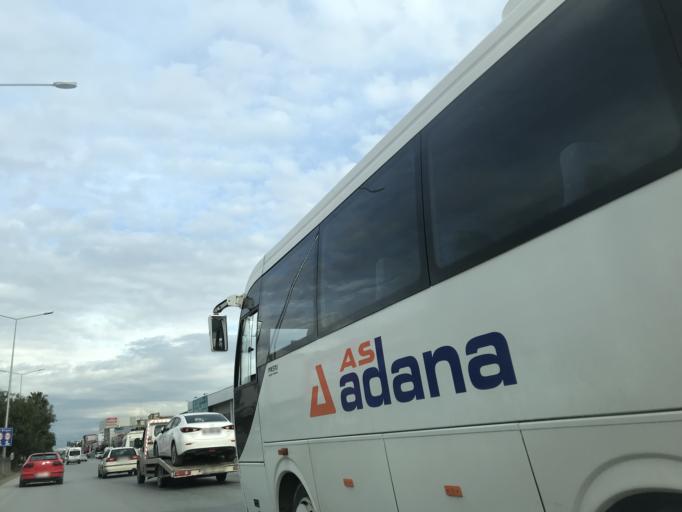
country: TR
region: Adana
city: Seyhan
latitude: 36.9951
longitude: 35.2750
